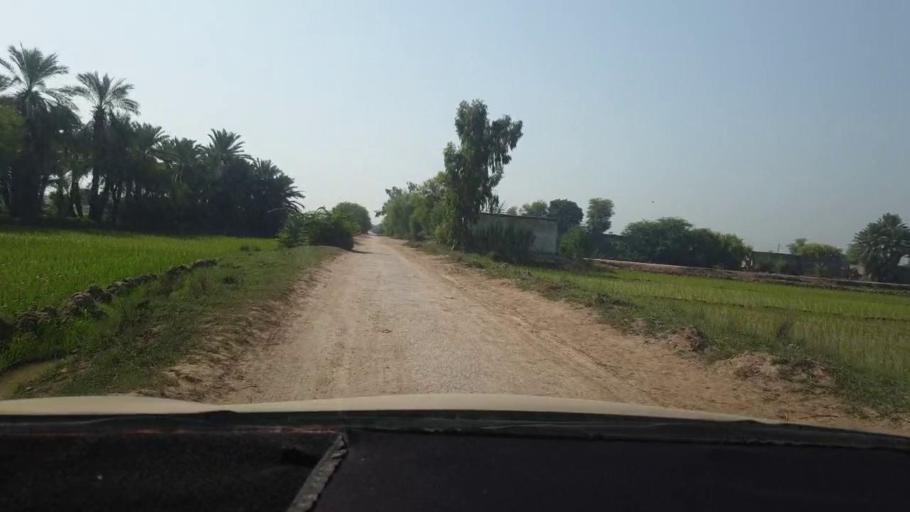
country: PK
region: Sindh
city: Miro Khan
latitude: 27.7263
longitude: 68.1201
